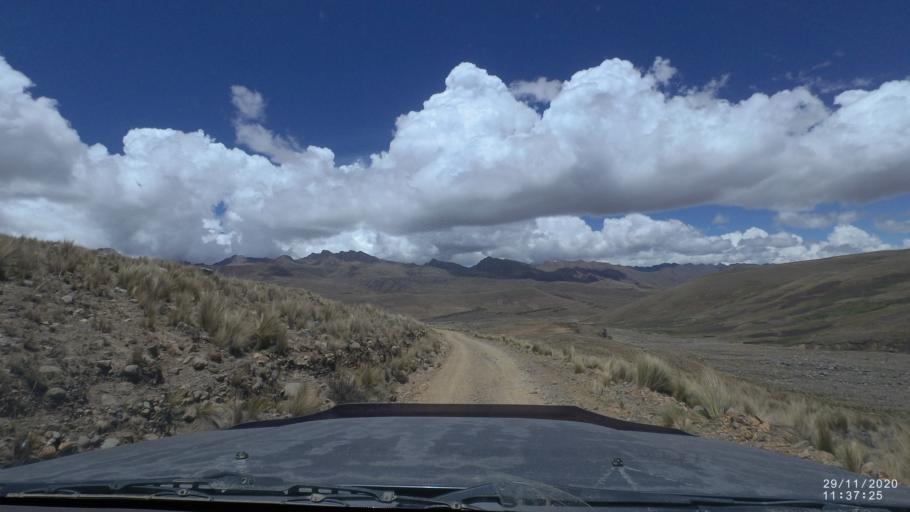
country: BO
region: Cochabamba
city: Cochabamba
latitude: -17.1973
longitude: -66.2323
